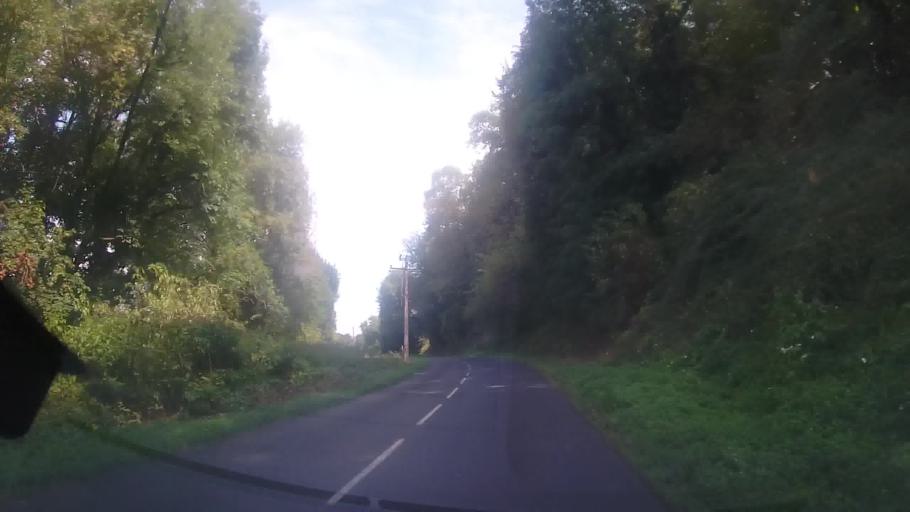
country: FR
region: Aquitaine
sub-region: Departement de la Dordogne
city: Carsac-Aillac
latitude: 44.8434
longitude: 1.3240
